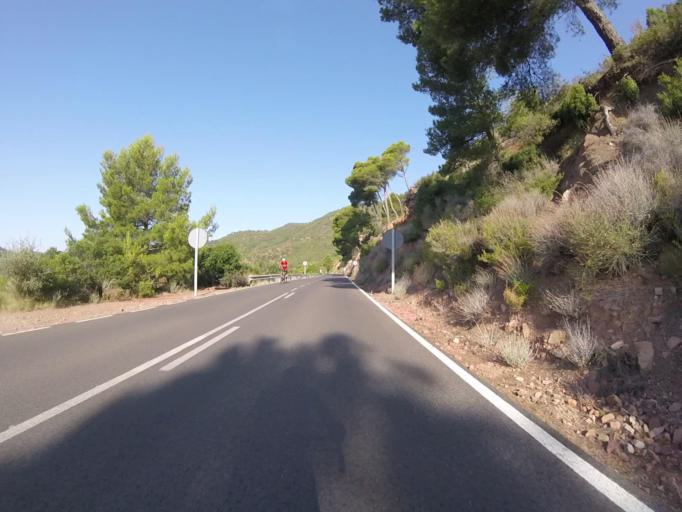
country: ES
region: Valencia
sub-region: Provincia de Castello
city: Benicassim
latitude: 40.0781
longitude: 0.0364
